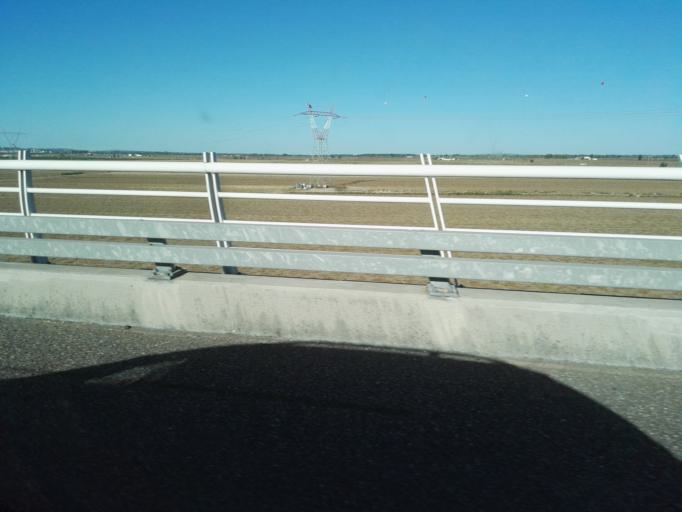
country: PT
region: Santarem
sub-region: Benavente
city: Samora Correia
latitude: 38.9869
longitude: -8.8907
